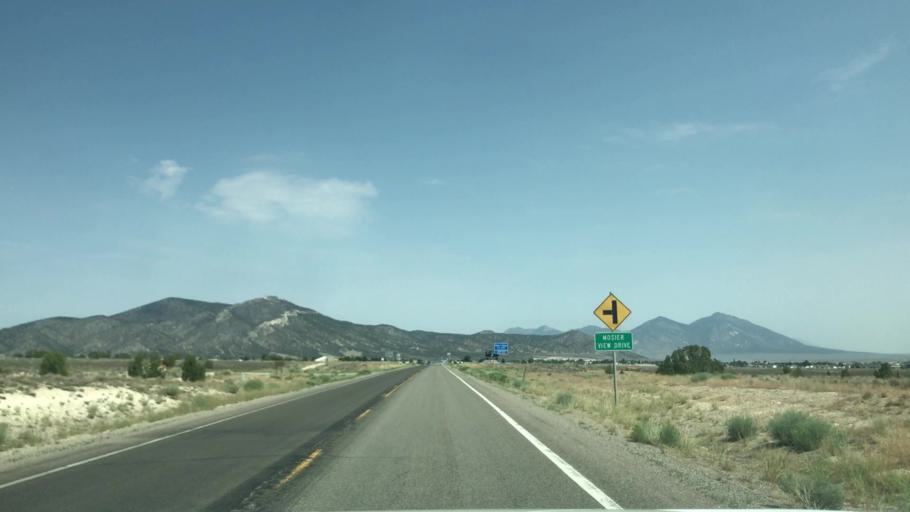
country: US
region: Nevada
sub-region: White Pine County
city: Ely
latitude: 39.2221
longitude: -114.8578
